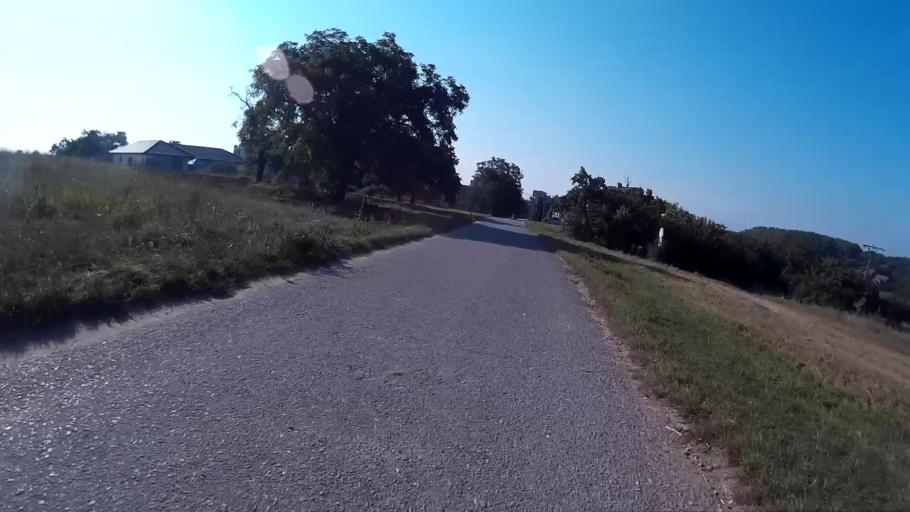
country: CZ
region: South Moravian
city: Vranovice
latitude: 48.9339
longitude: 16.5762
